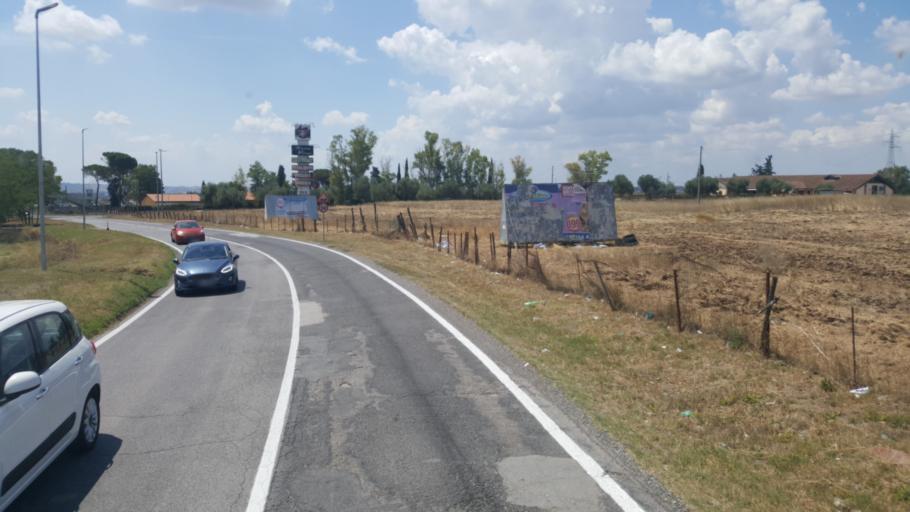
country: IT
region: Latium
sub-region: Citta metropolitana di Roma Capitale
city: Bivio di Capanelle
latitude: 42.1343
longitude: 12.5979
